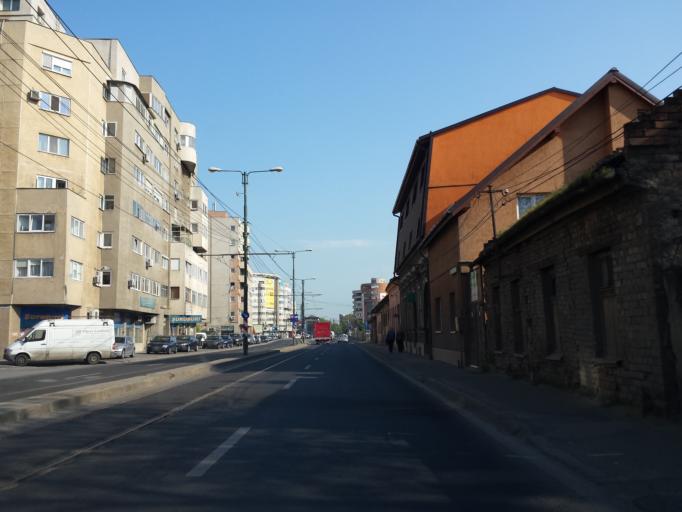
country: RO
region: Timis
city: Timisoara
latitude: 45.7632
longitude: 21.2608
